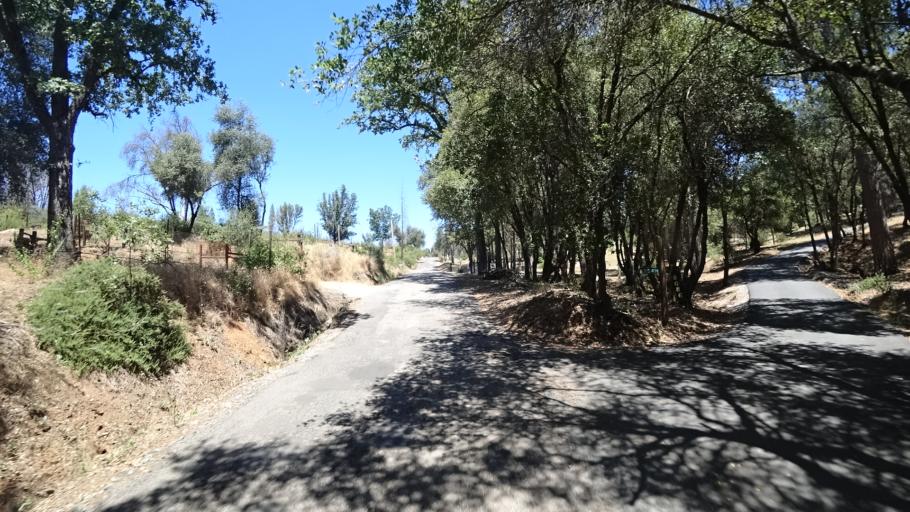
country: US
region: California
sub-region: Calaveras County
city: Mountain Ranch
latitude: 38.2356
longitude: -120.5469
